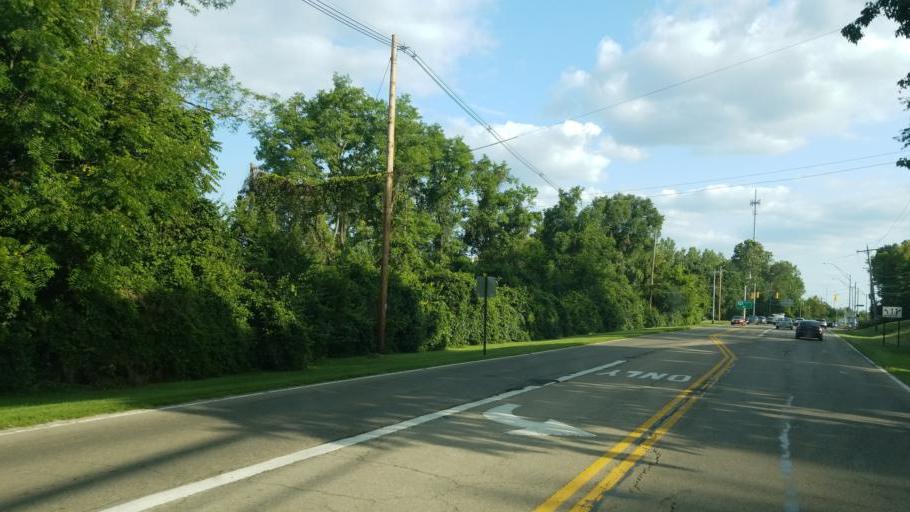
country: US
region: Ohio
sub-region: Franklin County
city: Worthington
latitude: 40.0566
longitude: -83.0341
